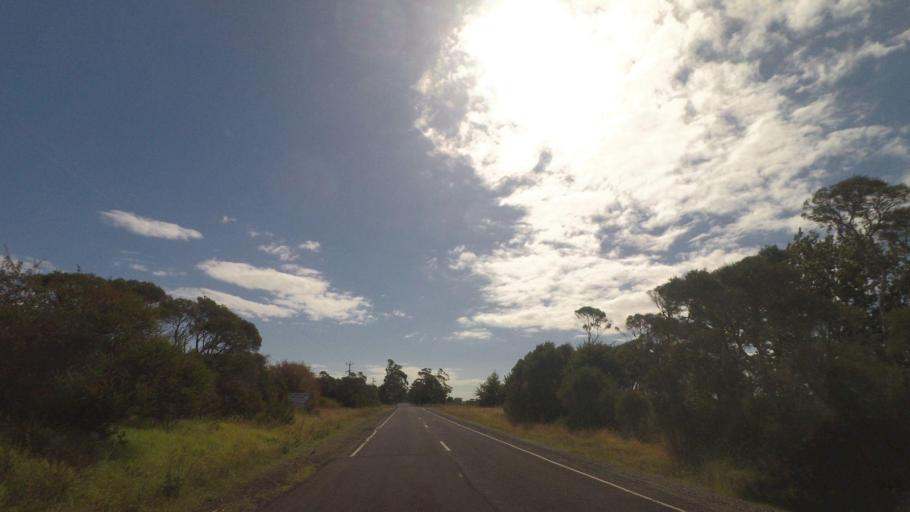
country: AU
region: Victoria
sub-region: Cardinia
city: Koo-Wee-Rup
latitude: -38.2481
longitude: 145.6383
